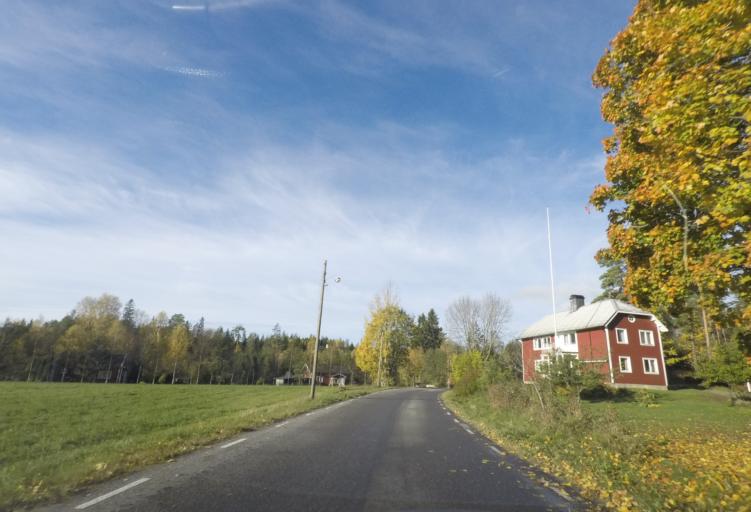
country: SE
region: OErebro
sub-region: Lindesbergs Kommun
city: Stora
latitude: 59.7759
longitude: 15.2856
